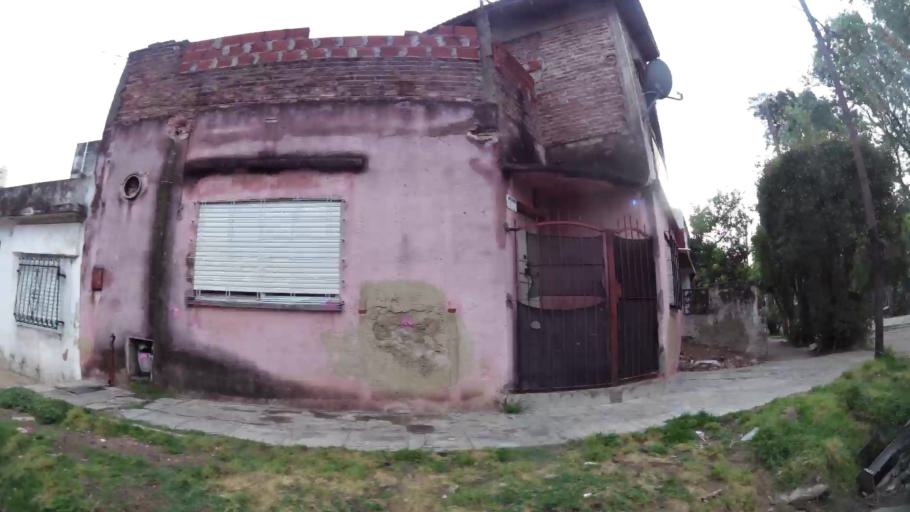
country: AR
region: Buenos Aires
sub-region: Partido de Lanus
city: Lanus
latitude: -34.7241
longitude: -58.3392
